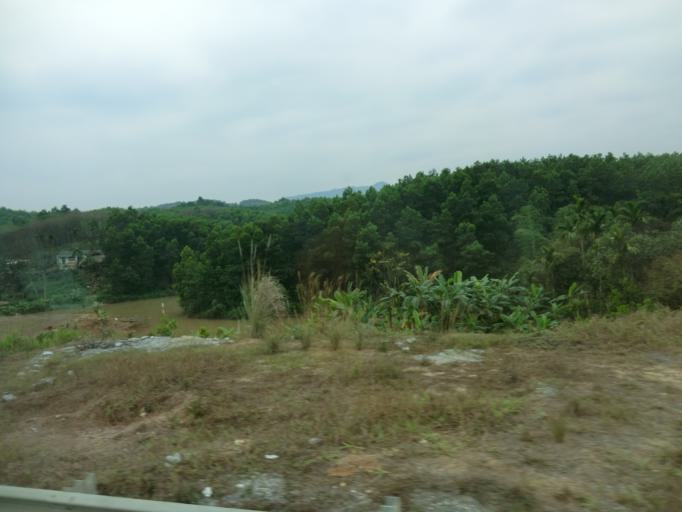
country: VN
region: Yen Bai
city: Co Phuc
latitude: 21.7147
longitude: 104.8335
